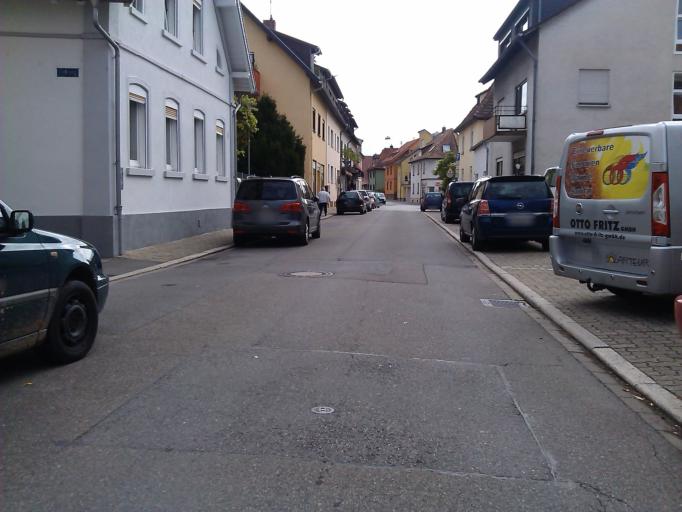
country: DE
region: Baden-Wuerttemberg
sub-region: Karlsruhe Region
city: Schriesheim
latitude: 49.4734
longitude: 8.6647
